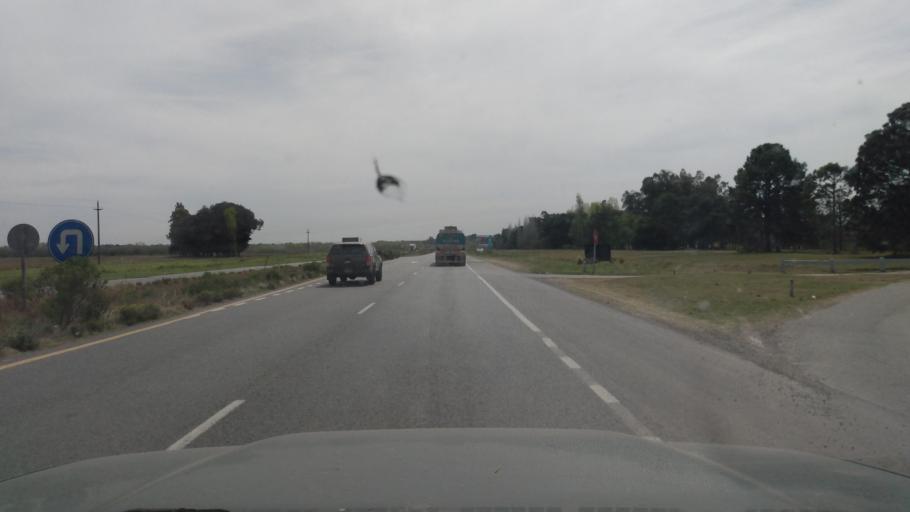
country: AR
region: Buenos Aires
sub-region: Partido de Lujan
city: Lujan
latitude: -34.5311
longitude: -59.0372
